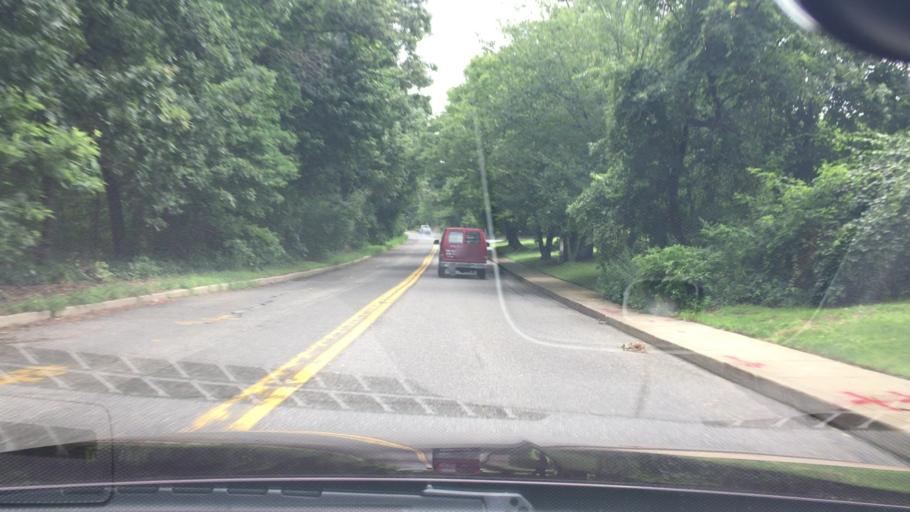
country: US
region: New York
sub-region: Suffolk County
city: Brentwood
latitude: 40.8228
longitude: -73.2545
